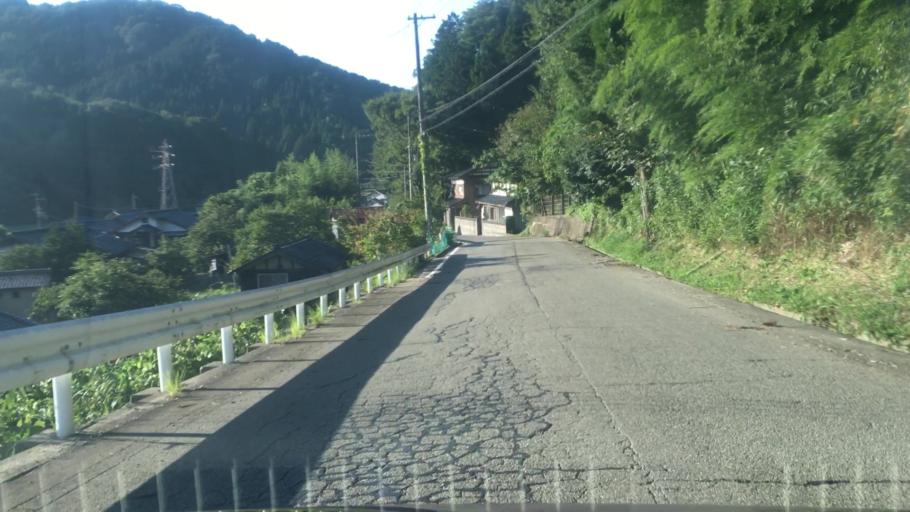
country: JP
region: Hyogo
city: Toyooka
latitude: 35.6098
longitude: 134.8309
